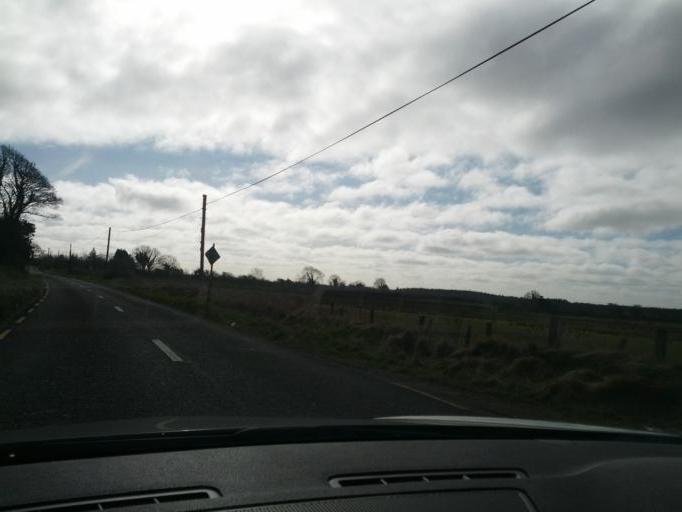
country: IE
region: Connaught
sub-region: County Galway
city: Ballinasloe
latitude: 53.4268
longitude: -8.4113
